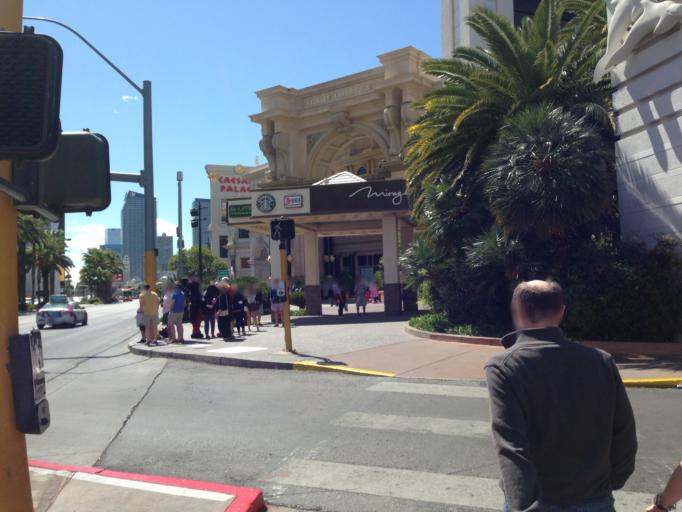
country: US
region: Nevada
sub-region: Clark County
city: Paradise
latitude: 36.1202
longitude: -115.1725
